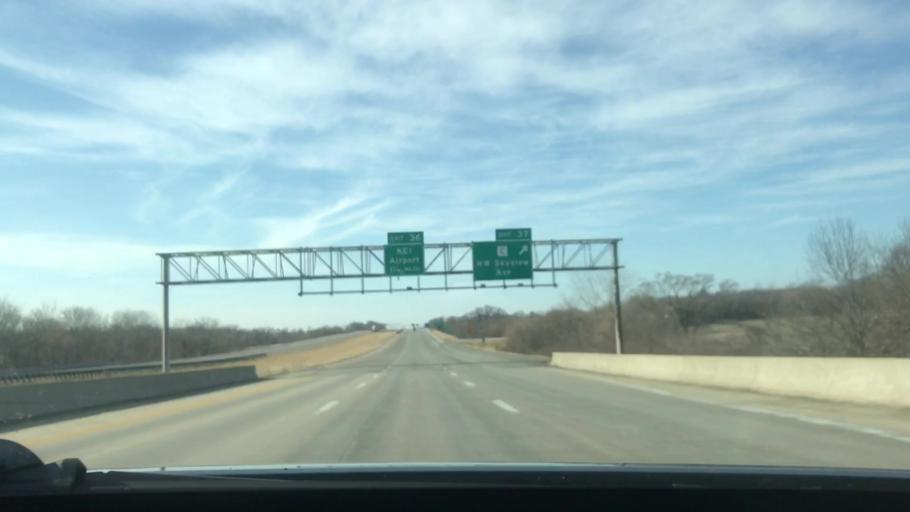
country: US
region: Missouri
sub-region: Platte County
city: Weatherby Lake
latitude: 39.3077
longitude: -94.6421
